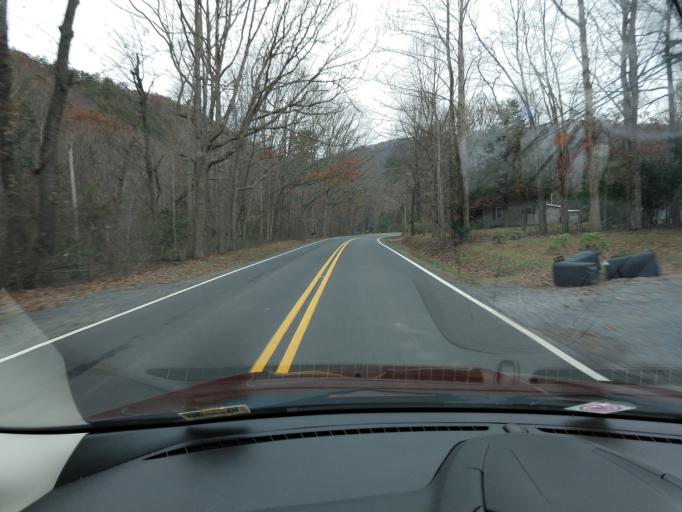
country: US
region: West Virginia
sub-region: Greenbrier County
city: White Sulphur Springs
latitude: 37.7248
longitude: -80.2127
